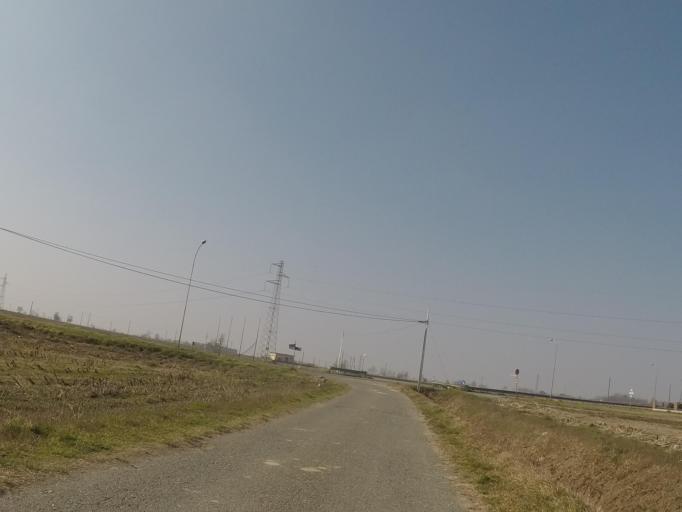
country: IT
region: Lombardy
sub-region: Provincia di Pavia
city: Mortara
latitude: 45.2548
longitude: 8.7271
